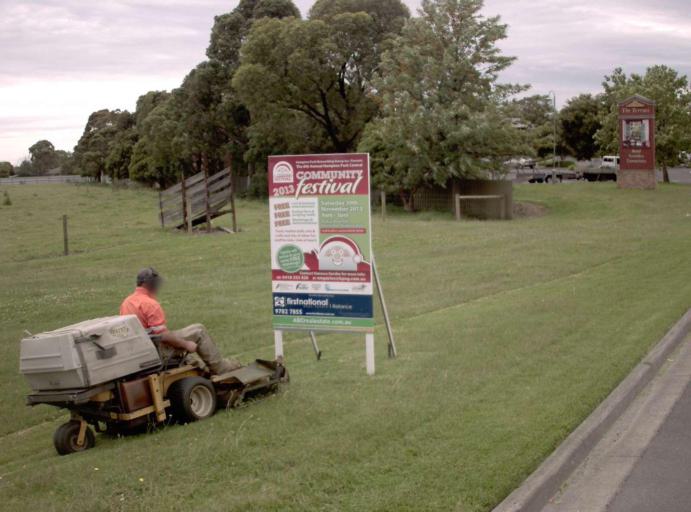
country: AU
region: Victoria
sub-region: Casey
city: Cranbourne
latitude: -38.0965
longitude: 145.2828
